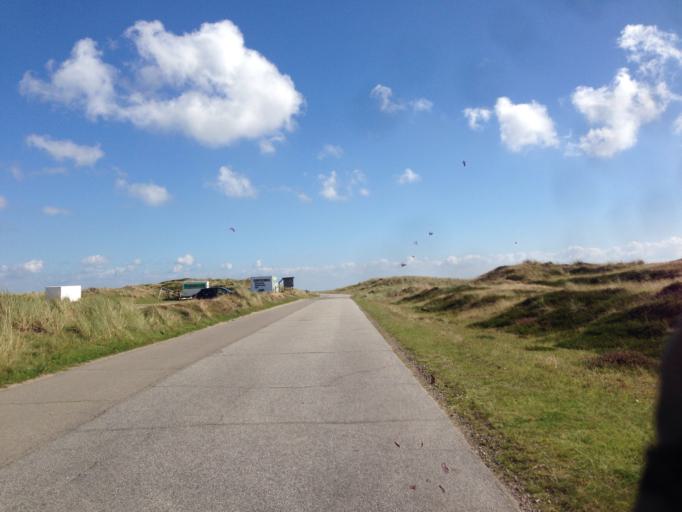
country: DE
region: Schleswig-Holstein
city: List
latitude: 55.0497
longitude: 8.4258
